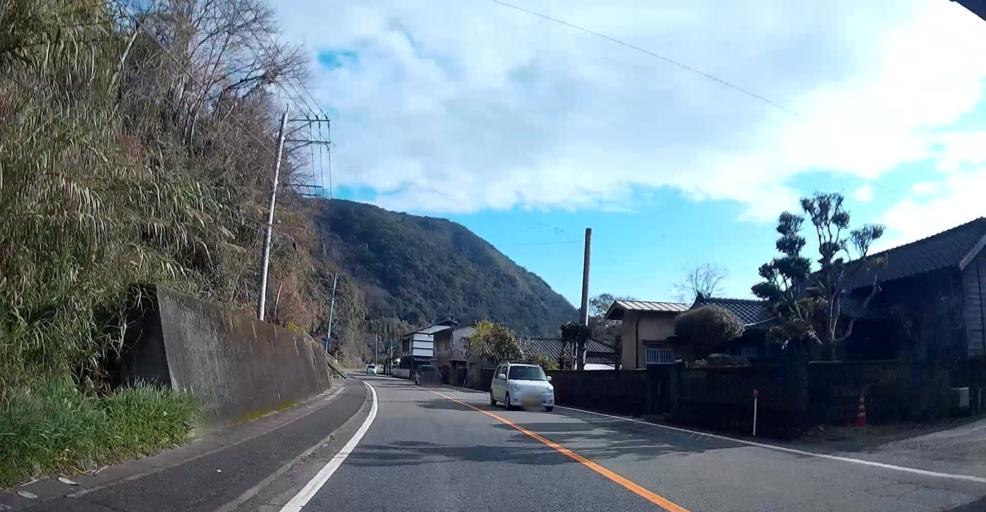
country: JP
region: Kumamoto
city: Yatsushiro
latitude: 32.6190
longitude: 130.4597
